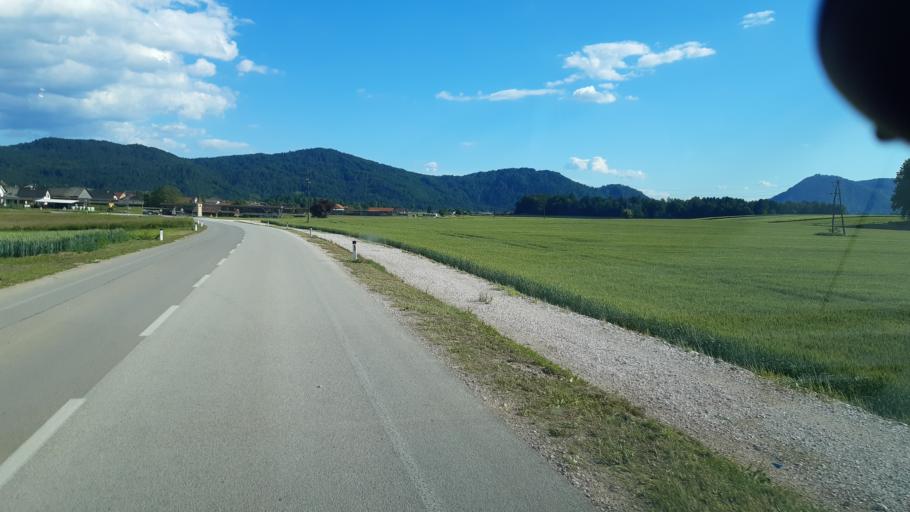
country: SI
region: Vodice
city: Vodice
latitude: 46.1792
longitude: 14.5032
